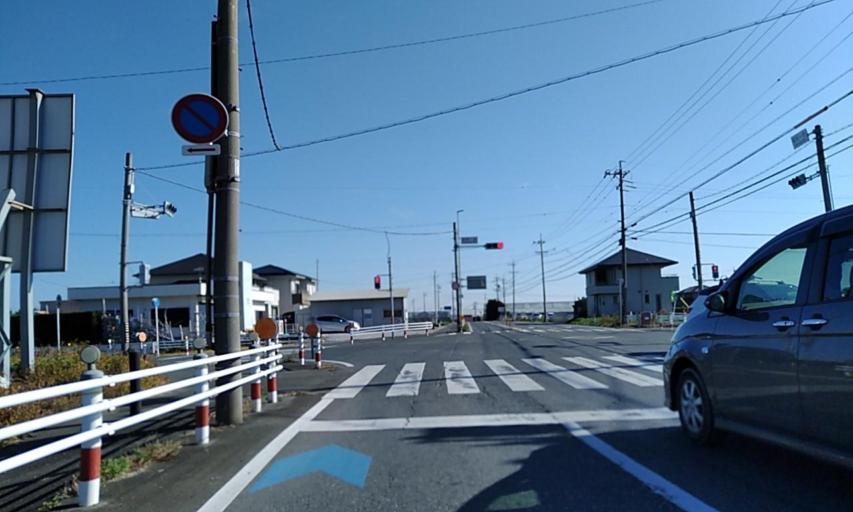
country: JP
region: Aichi
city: Tahara
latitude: 34.6205
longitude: 137.2257
